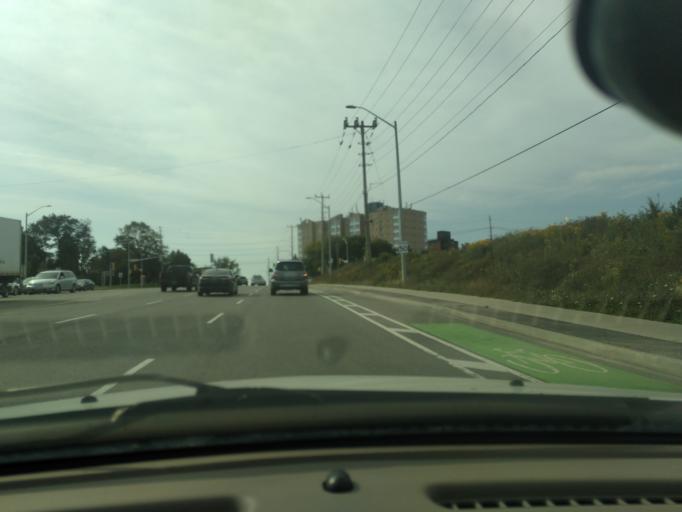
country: CA
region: Ontario
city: Barrie
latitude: 44.4120
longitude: -79.6736
